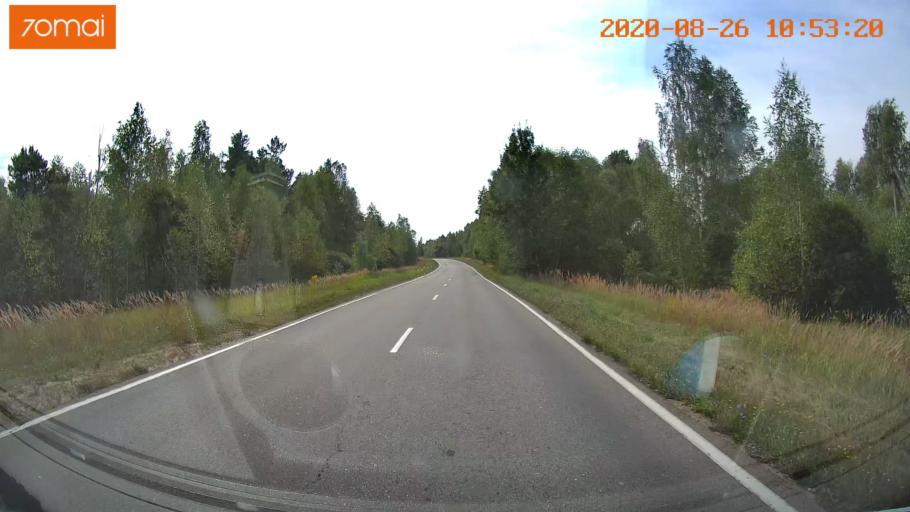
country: RU
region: Rjazan
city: Lashma
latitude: 54.6431
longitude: 41.1519
